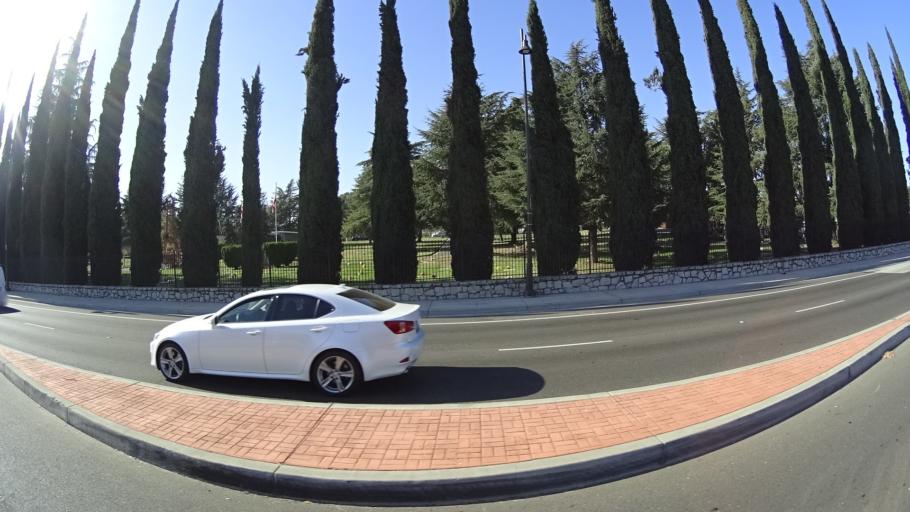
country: US
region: California
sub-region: Sacramento County
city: Citrus Heights
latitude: 38.7005
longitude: -121.2903
